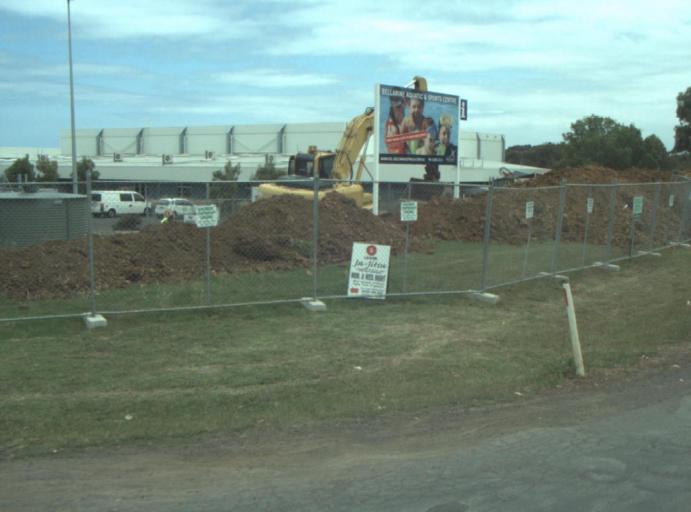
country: AU
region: Victoria
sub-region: Greater Geelong
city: Leopold
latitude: -38.2605
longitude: 144.5445
